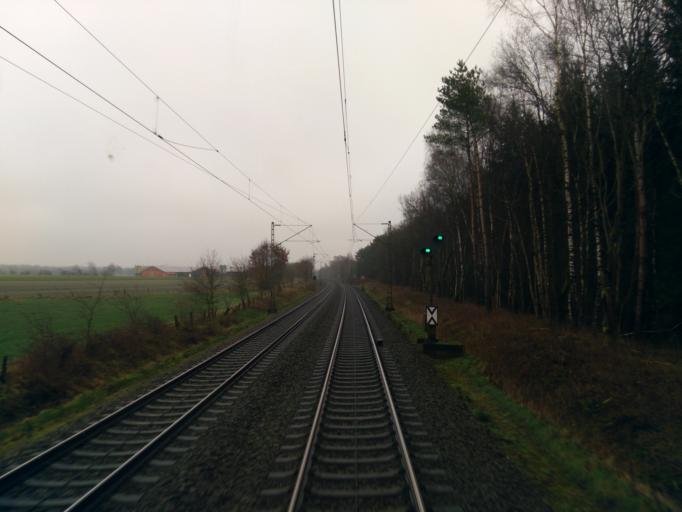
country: DE
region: Lower Saxony
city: Botersen
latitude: 53.1027
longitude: 9.3113
